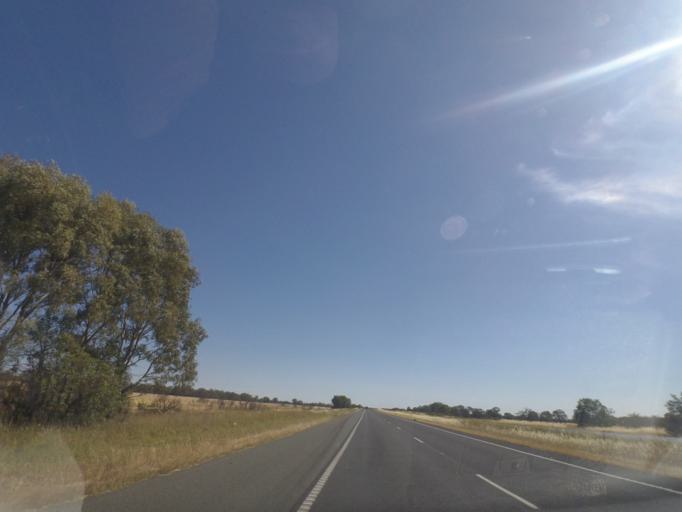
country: AU
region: Victoria
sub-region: Greater Shepparton
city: Shepparton
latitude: -36.6243
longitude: 145.3015
